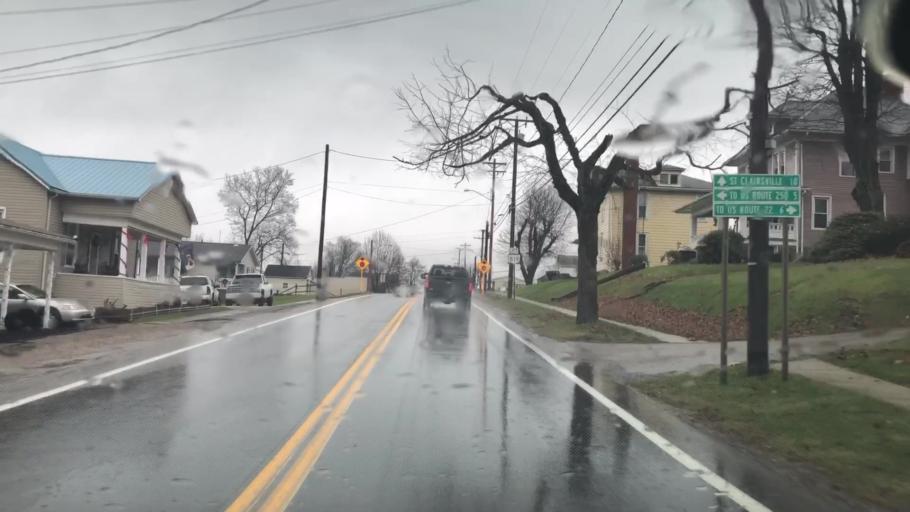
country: US
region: Ohio
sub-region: Harrison County
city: Cadiz
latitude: 40.1860
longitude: -80.9958
